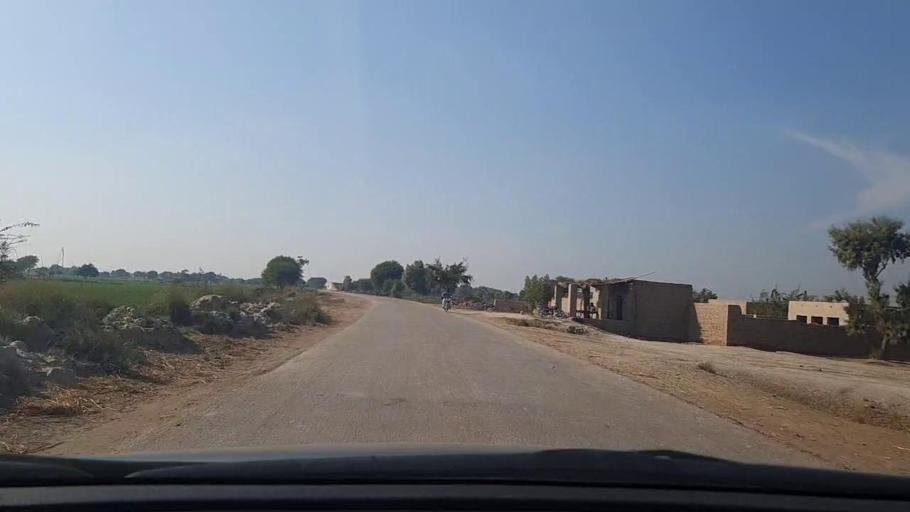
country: PK
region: Sindh
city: Daulatpur
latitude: 26.3148
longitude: 68.0678
